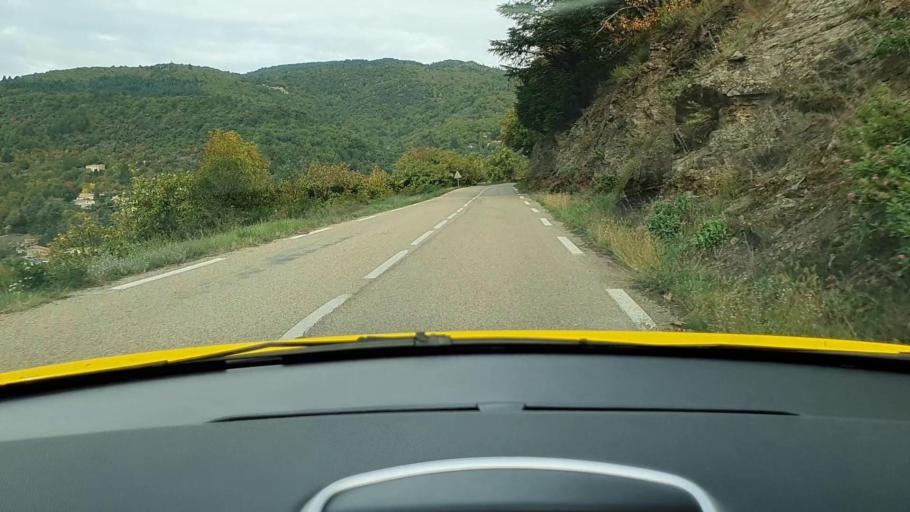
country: FR
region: Languedoc-Roussillon
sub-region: Departement du Gard
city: Le Vigan
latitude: 43.9984
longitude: 3.5892
